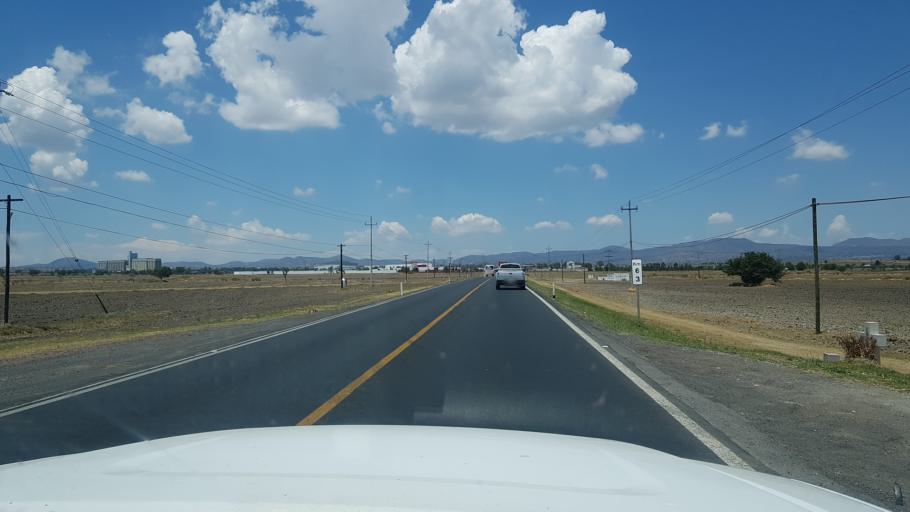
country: MX
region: Hidalgo
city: Calpulalpan
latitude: 19.5806
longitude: -98.5291
